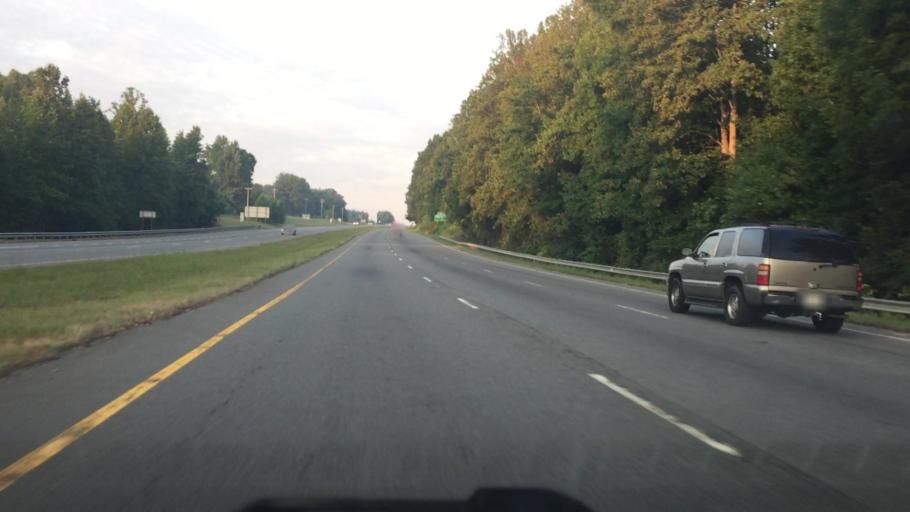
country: US
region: North Carolina
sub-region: Guilford County
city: McLeansville
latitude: 36.1728
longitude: -79.7139
